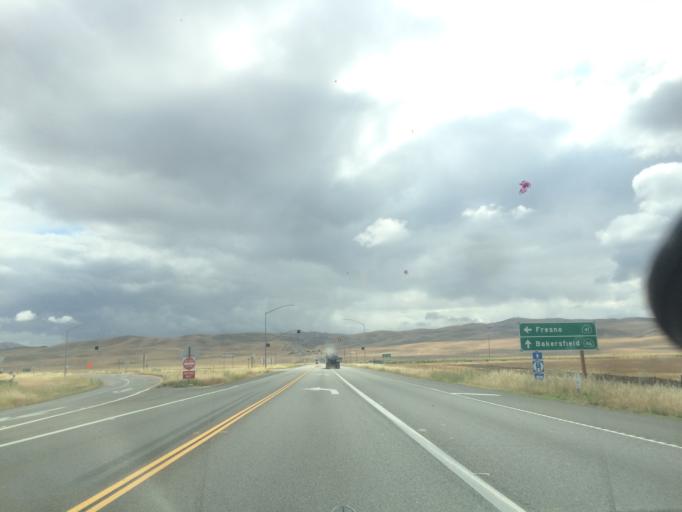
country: US
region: California
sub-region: San Luis Obispo County
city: Shandon
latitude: 35.7342
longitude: -120.2860
